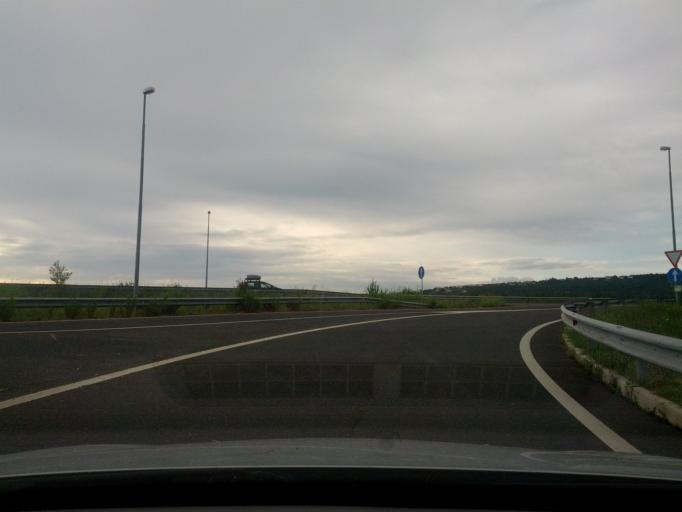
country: SI
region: Koper-Capodistria
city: Prade
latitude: 45.5564
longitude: 13.7806
